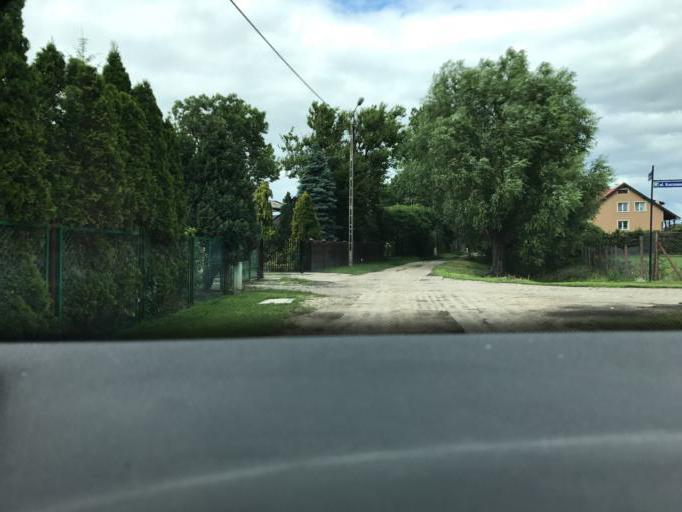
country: PL
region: Pomeranian Voivodeship
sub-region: Powiat gdanski
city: Pruszcz Gdanski
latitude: 54.2754
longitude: 18.6915
